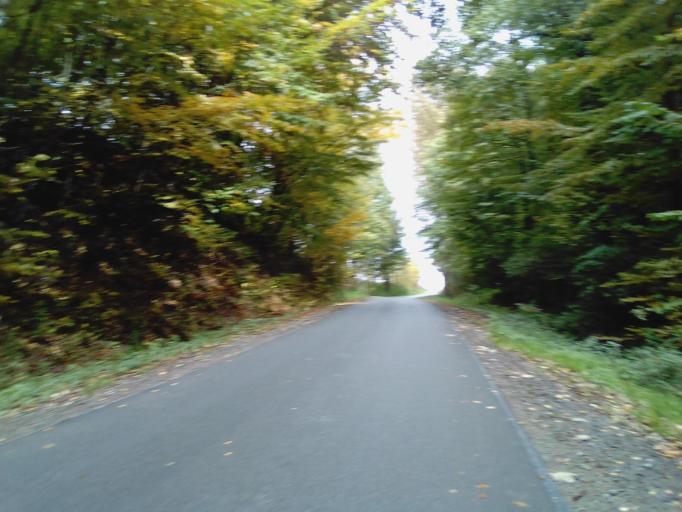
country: PL
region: Subcarpathian Voivodeship
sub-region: Powiat strzyzowski
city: Gwoznica Gorna
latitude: 49.8339
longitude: 22.0048
